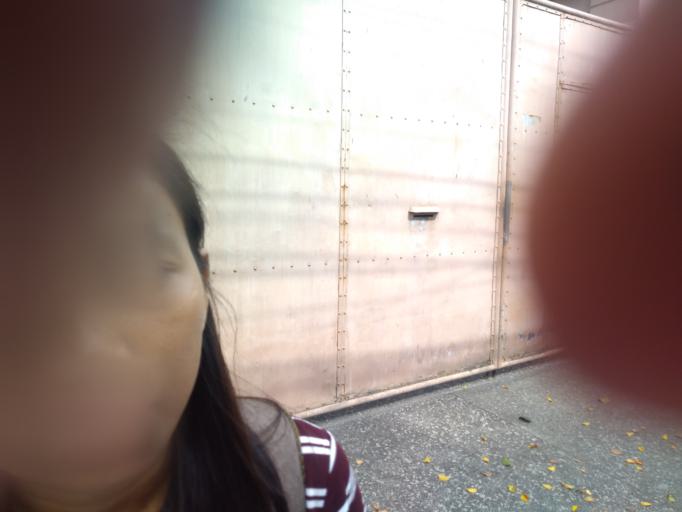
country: PH
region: Central Visayas
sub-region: Province of Negros Oriental
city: Dumaguete
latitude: 9.3023
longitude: 123.2980
